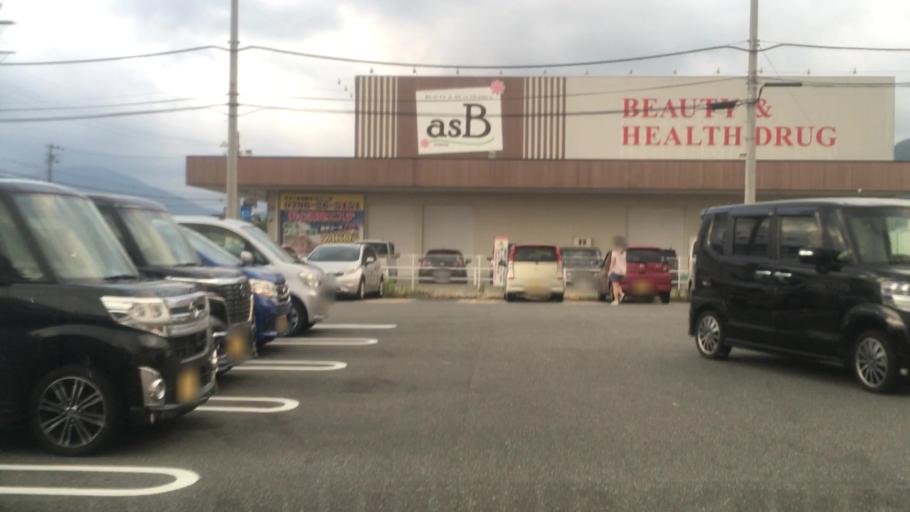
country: JP
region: Hyogo
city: Toyooka
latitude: 35.5555
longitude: 134.8159
